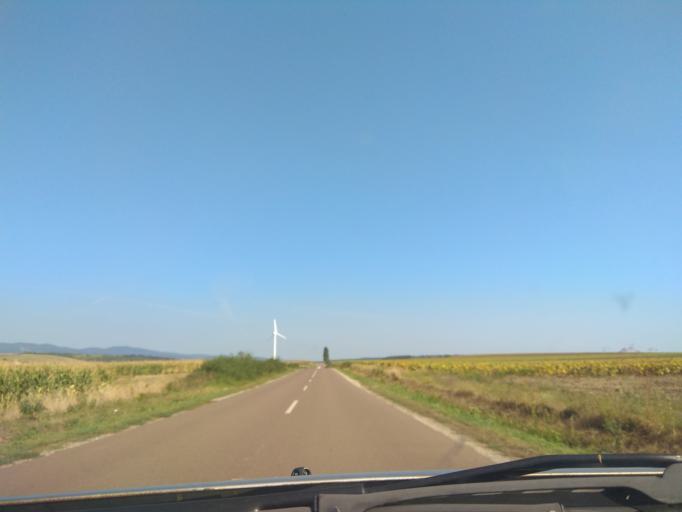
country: HU
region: Borsod-Abauj-Zemplen
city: Emod
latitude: 47.9625
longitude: 20.8029
